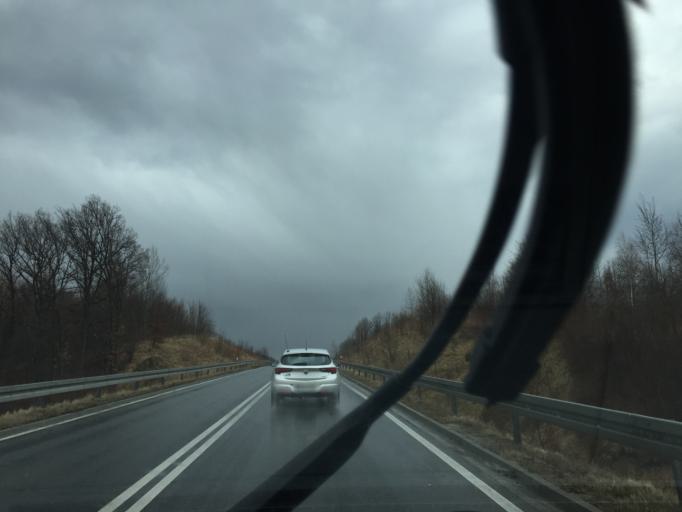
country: PL
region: Lesser Poland Voivodeship
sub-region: Powiat suski
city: Zembrzyce
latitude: 49.7700
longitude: 19.6042
